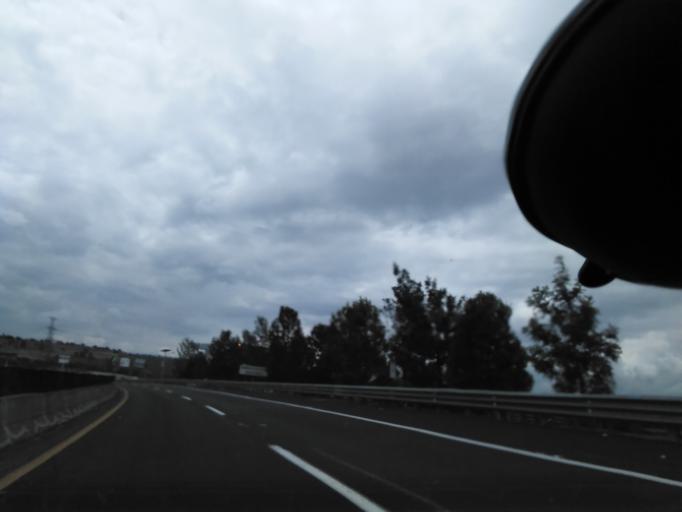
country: MX
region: Mexico
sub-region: Huehuetoca
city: Jorobas
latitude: 19.8237
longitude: -99.2343
